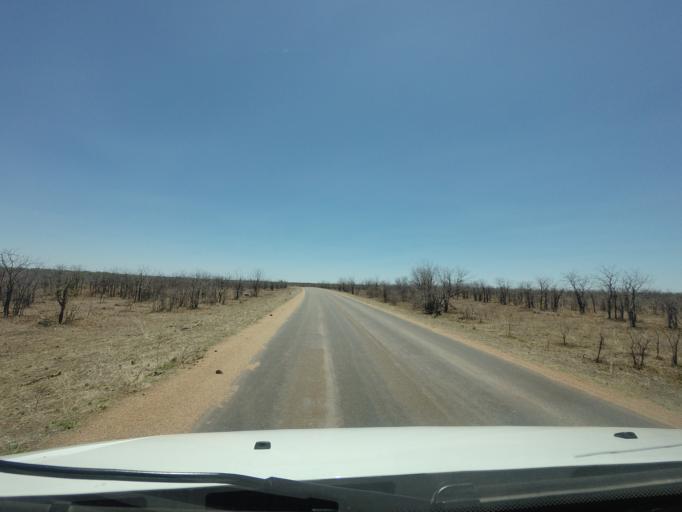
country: ZA
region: Limpopo
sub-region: Mopani District Municipality
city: Phalaborwa
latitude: -23.5650
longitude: 31.4523
